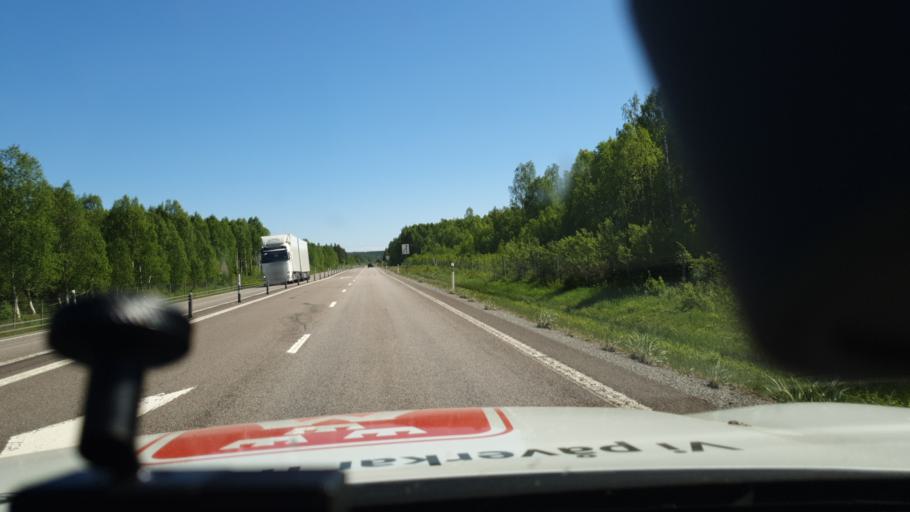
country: SE
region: Norrbotten
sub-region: Kalix Kommun
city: Toere
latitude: 65.8965
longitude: 22.8844
